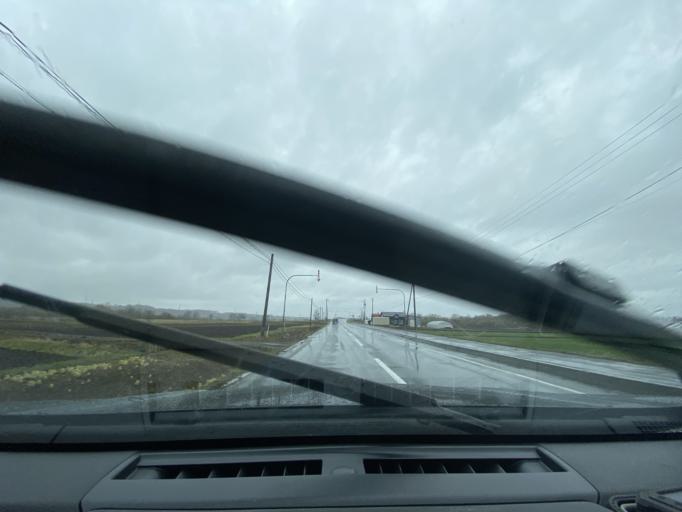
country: JP
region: Hokkaido
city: Fukagawa
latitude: 43.8090
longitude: 142.0189
